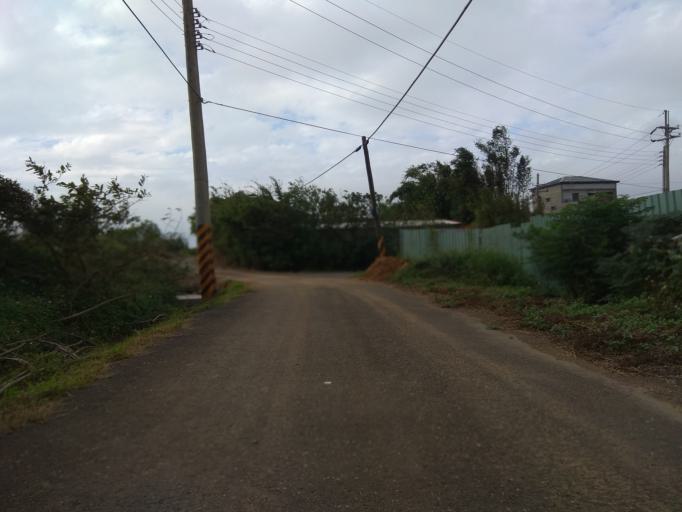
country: TW
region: Taiwan
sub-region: Hsinchu
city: Zhubei
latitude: 24.9713
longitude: 121.0432
